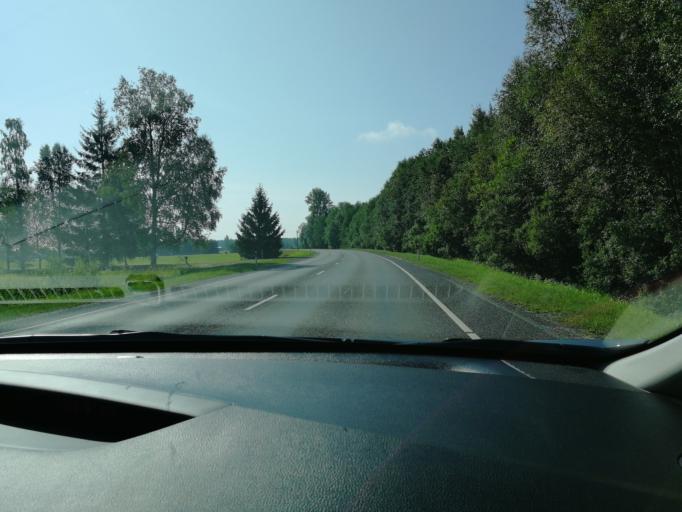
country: EE
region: Paernumaa
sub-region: Paikuse vald
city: Paikuse
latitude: 58.2054
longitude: 24.7221
